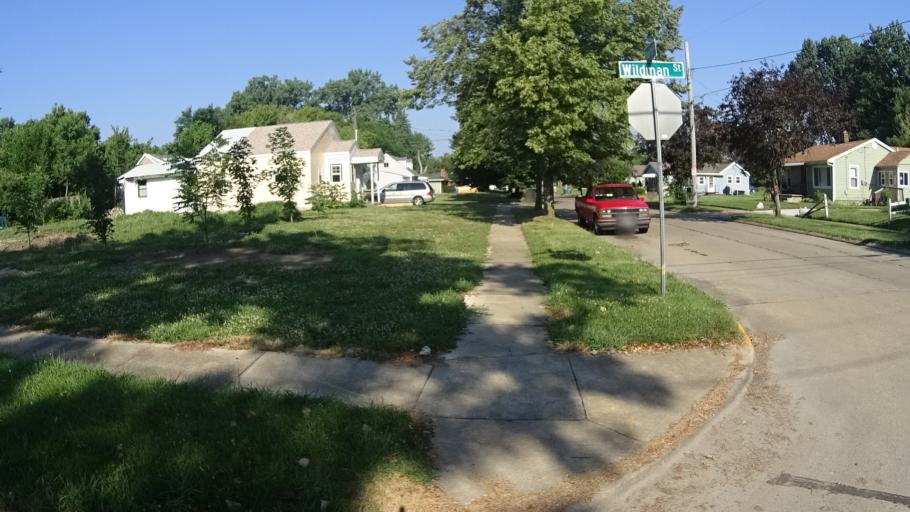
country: US
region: Ohio
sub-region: Erie County
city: Sandusky
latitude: 41.4482
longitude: -82.6808
